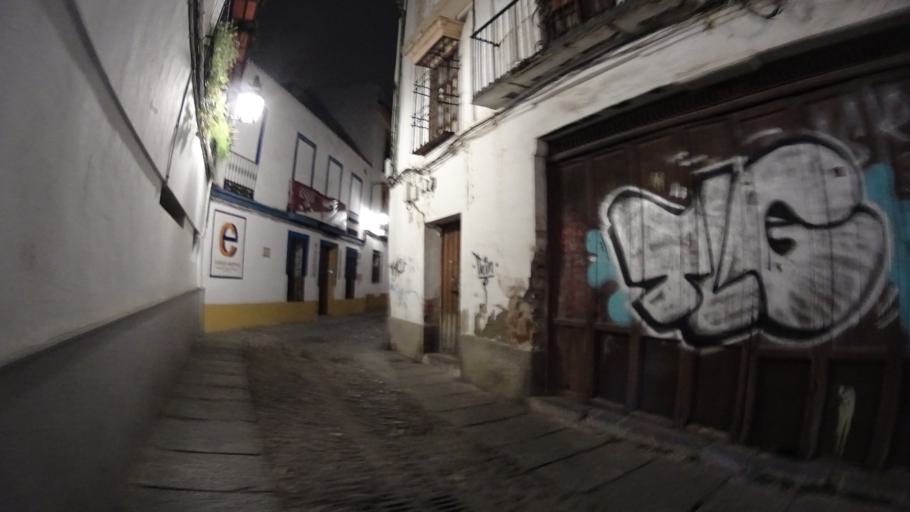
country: ES
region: Andalusia
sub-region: Province of Cordoba
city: Cordoba
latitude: 37.8822
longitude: -4.7747
